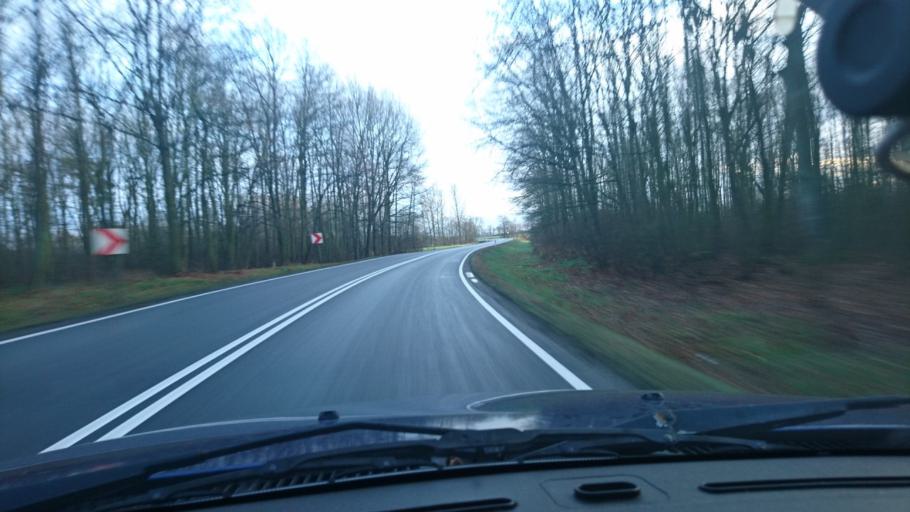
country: PL
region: Opole Voivodeship
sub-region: Powiat kluczborski
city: Byczyna
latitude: 51.1460
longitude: 18.1905
